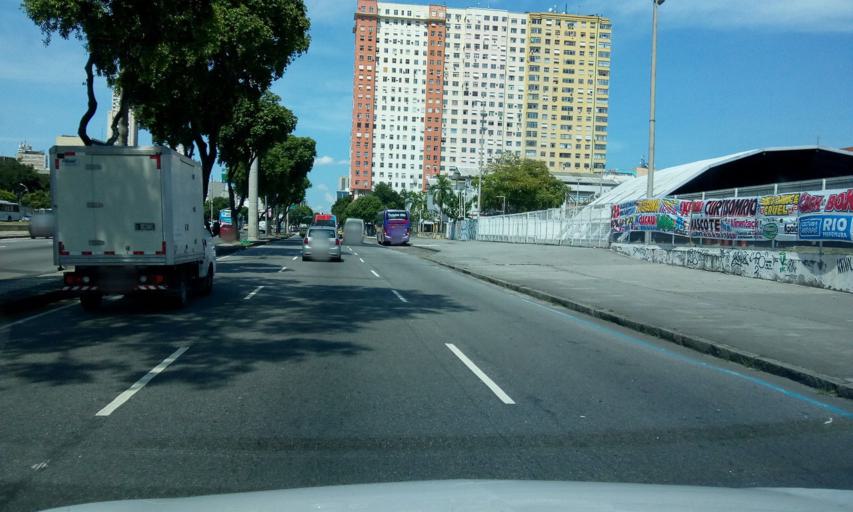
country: BR
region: Rio de Janeiro
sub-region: Rio De Janeiro
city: Rio de Janeiro
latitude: -22.9073
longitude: -43.1967
